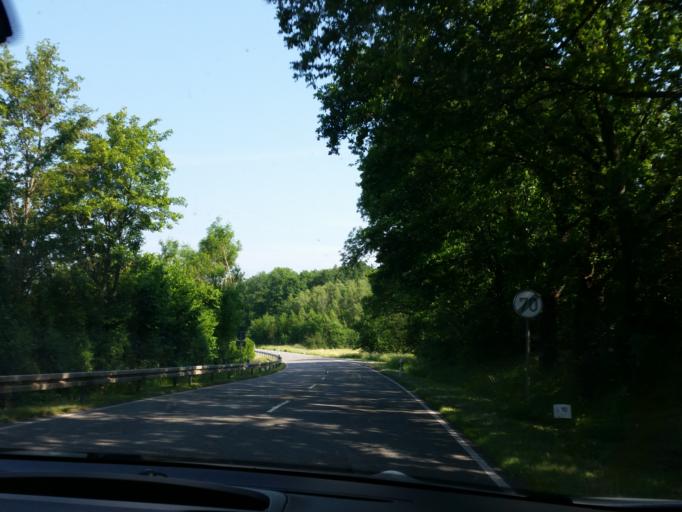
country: DE
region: Saarland
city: Weiskirchen
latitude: 49.5075
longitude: 6.8290
